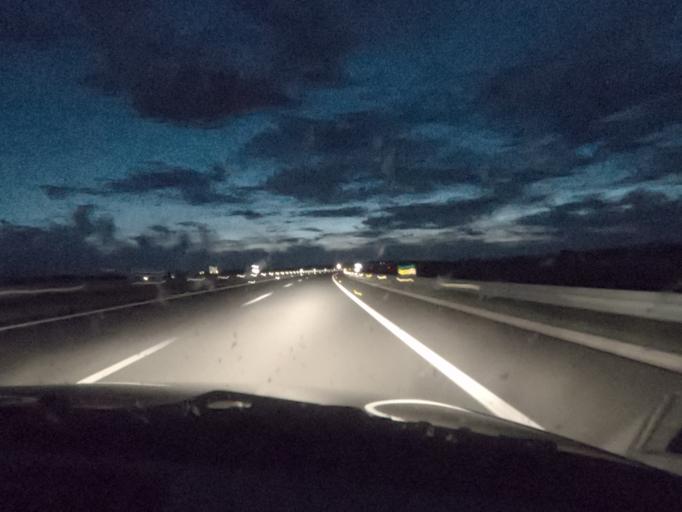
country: ES
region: Extremadura
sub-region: Provincia de Caceres
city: Morcillo
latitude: 39.9743
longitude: -6.3601
